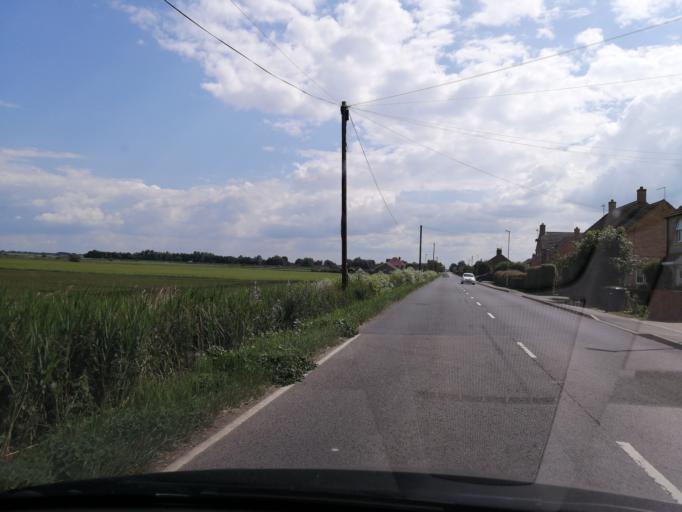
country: GB
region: England
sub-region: Cambridgeshire
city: Ramsey
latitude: 52.4765
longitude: -0.1526
